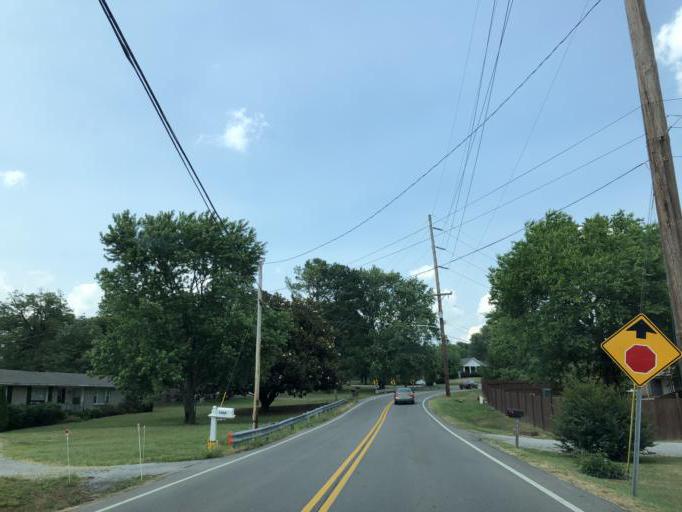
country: US
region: Tennessee
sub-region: Davidson County
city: Goodlettsville
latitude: 36.2442
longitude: -86.7314
